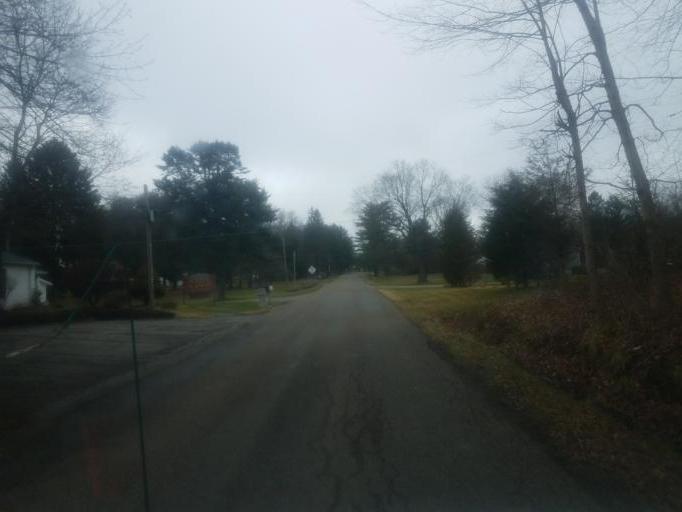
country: US
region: Ohio
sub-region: Richland County
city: Lexington
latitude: 40.6724
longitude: -82.5278
